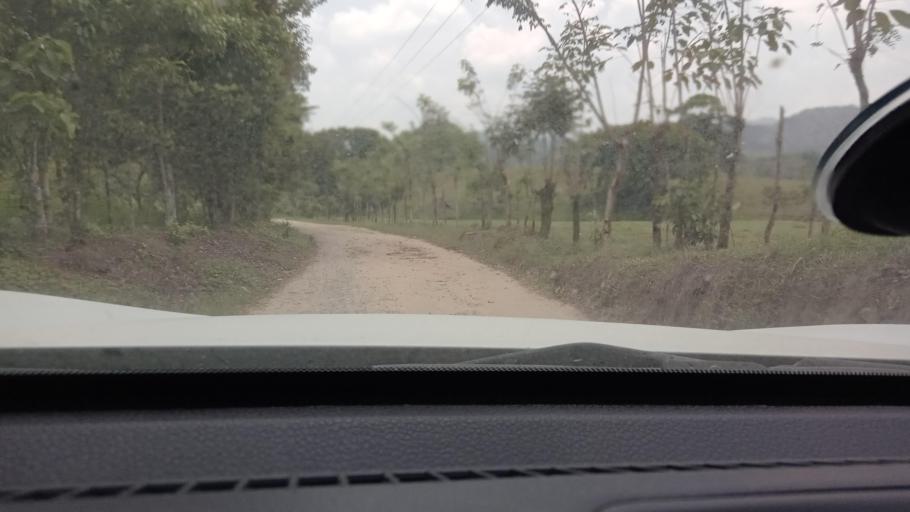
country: MX
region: Tabasco
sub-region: Huimanguillo
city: Francisco Rueda
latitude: 17.5200
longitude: -93.8866
